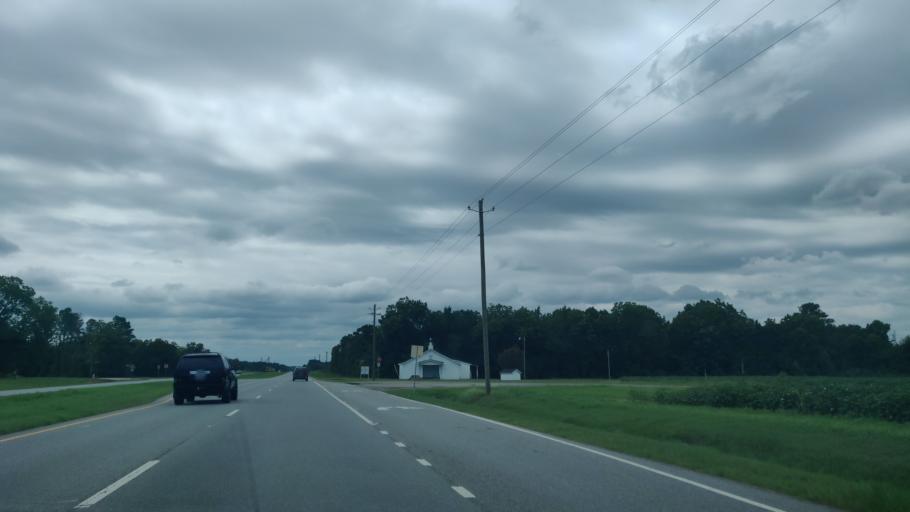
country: US
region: Georgia
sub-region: Terrell County
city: Dawson
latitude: 31.8210
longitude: -84.4595
